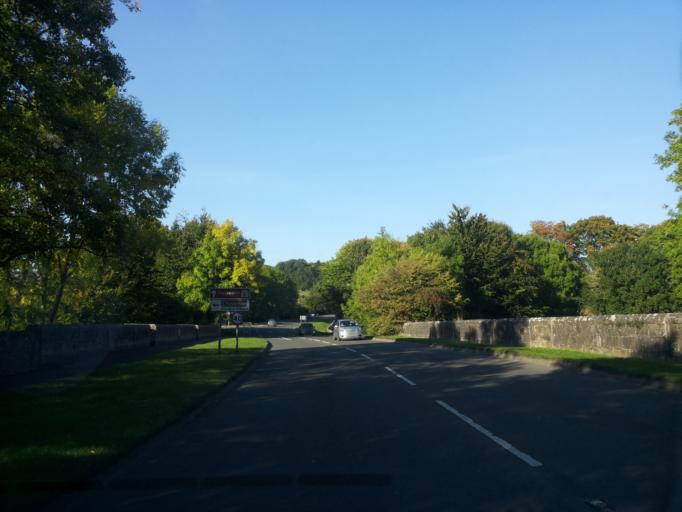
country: GB
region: England
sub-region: Derbyshire
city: Bakewell
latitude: 53.2228
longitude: -1.7057
